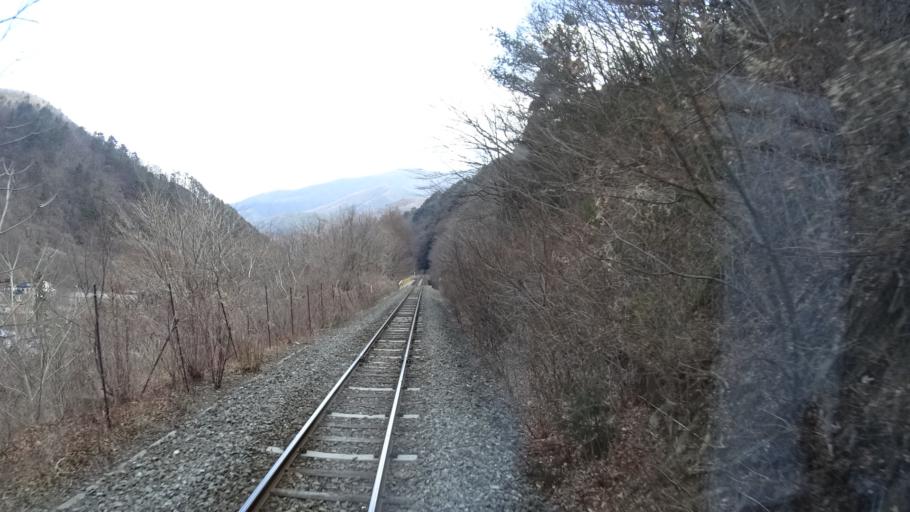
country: JP
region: Iwate
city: Kamaishi
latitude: 39.2612
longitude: 141.7295
